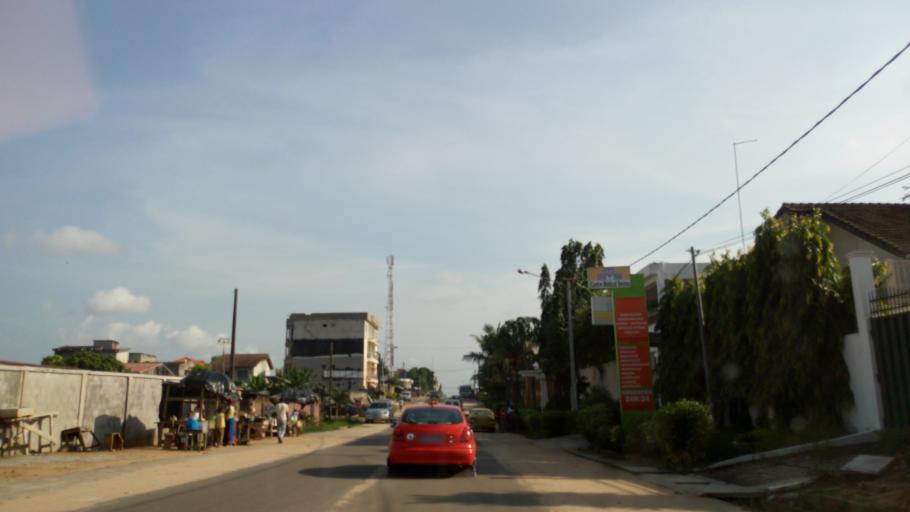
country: CI
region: Lagunes
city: Abobo
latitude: 5.3763
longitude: -3.9552
